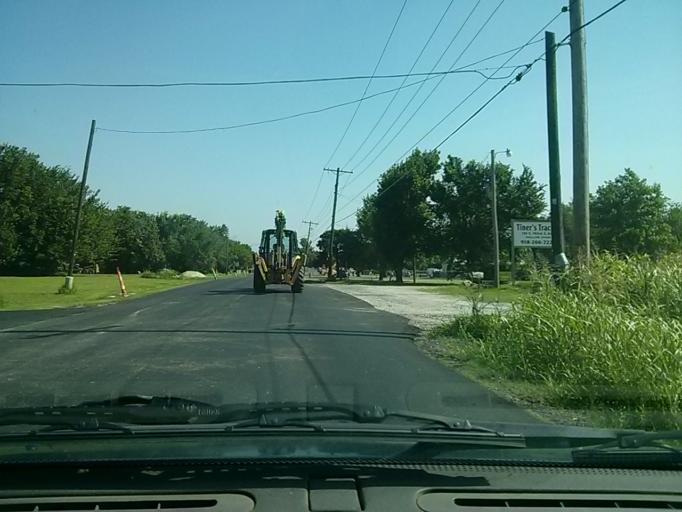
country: US
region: Oklahoma
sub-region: Rogers County
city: Catoosa
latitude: 36.1514
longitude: -95.7617
